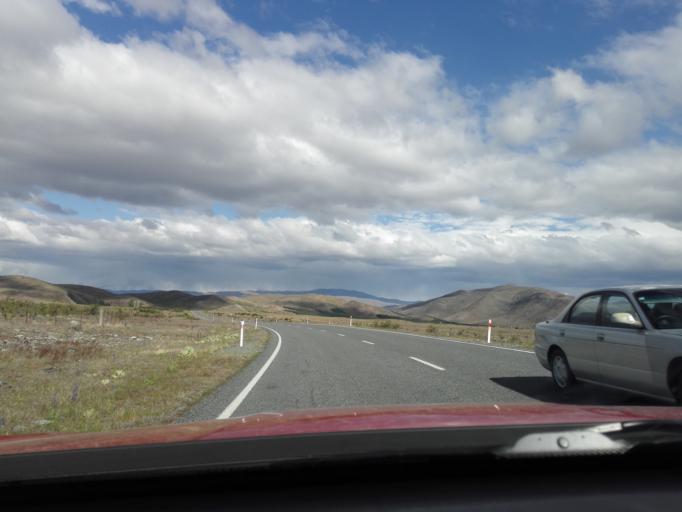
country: NZ
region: Canterbury
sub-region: Timaru District
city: Pleasant Point
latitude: -44.2015
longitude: 170.2528
